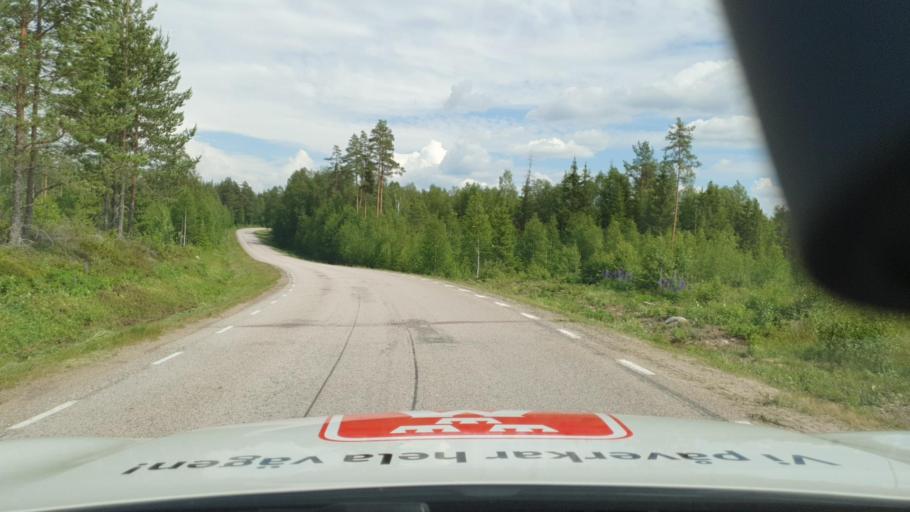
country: NO
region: Hedmark
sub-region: Asnes
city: Flisa
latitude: 60.6957
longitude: 12.4864
